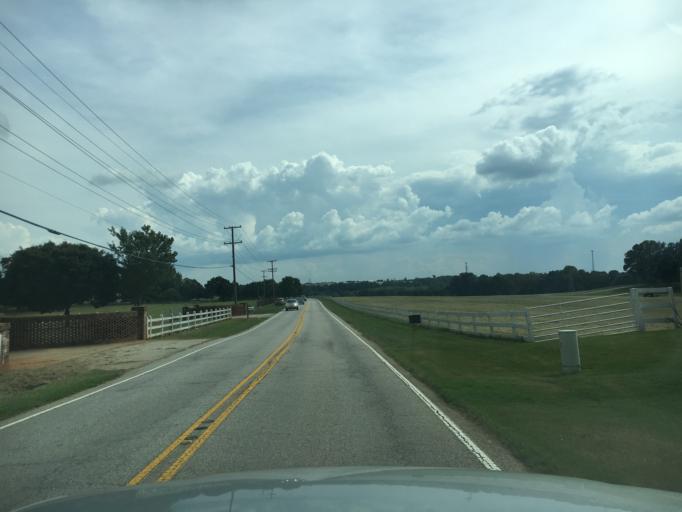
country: US
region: South Carolina
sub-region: Greenville County
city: Greer
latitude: 34.8821
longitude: -82.2419
